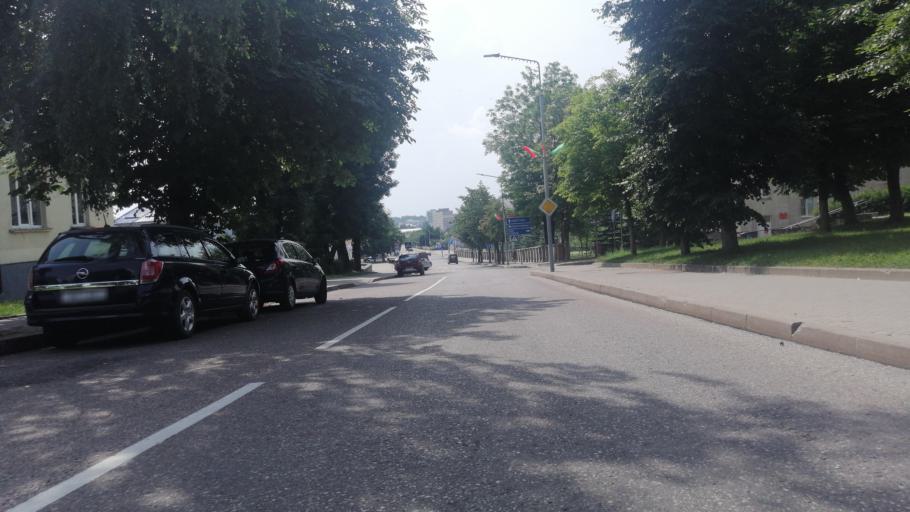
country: BY
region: Grodnenskaya
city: Navahrudak
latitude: 53.5929
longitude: 25.8202
